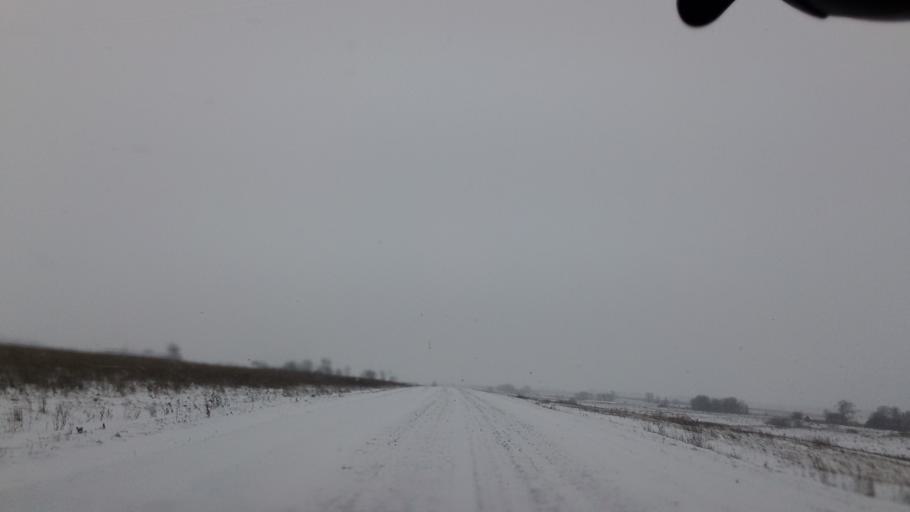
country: RU
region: Tula
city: Volovo
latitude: 53.6825
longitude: 37.9322
